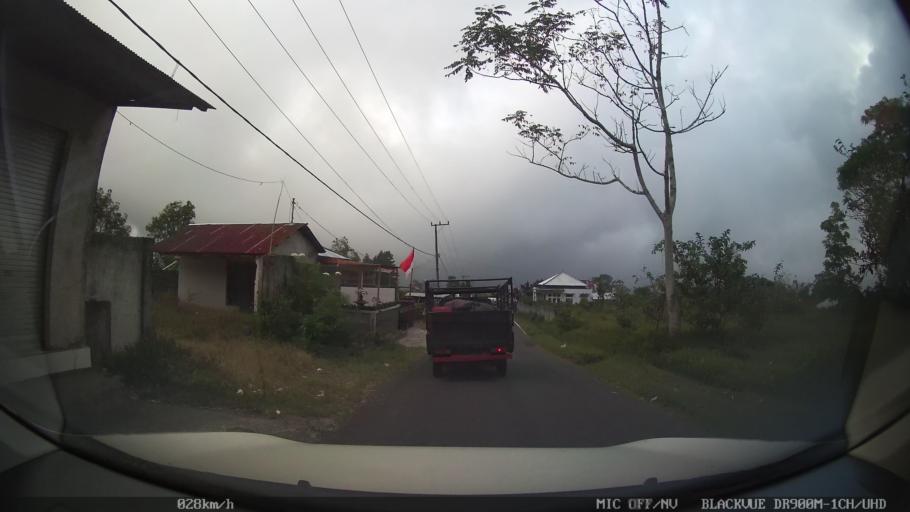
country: ID
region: Bali
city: Banjar Kedisan
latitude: -8.2711
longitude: 115.3307
